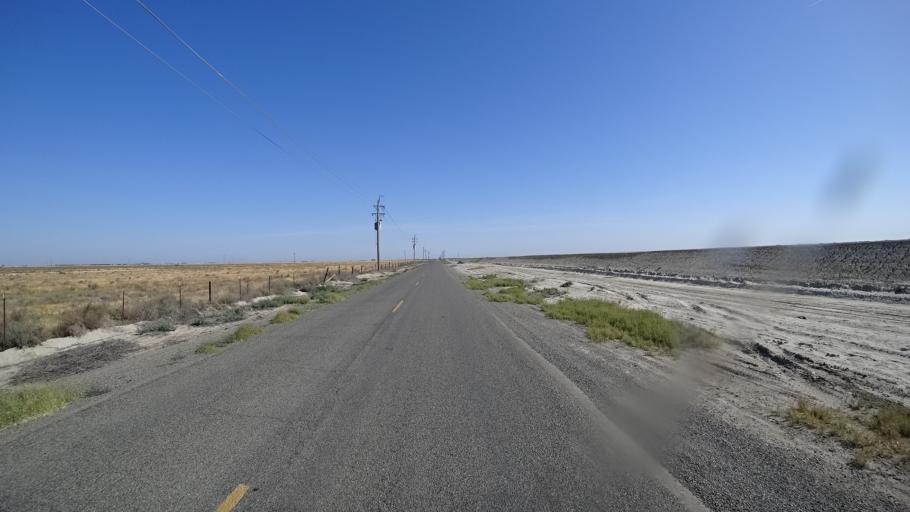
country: US
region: California
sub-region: Kings County
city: Corcoran
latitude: 36.1489
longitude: -119.5649
